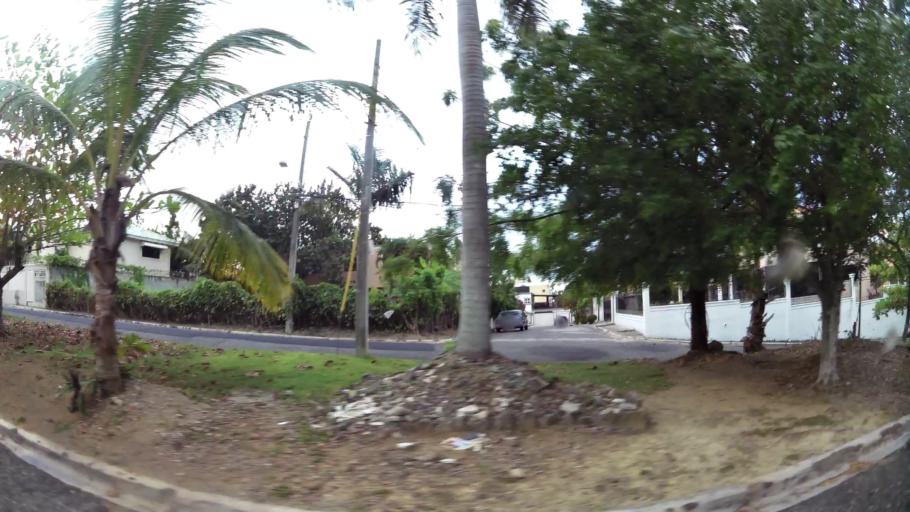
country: DO
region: Nacional
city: Santo Domingo
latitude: 18.4994
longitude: -69.9726
